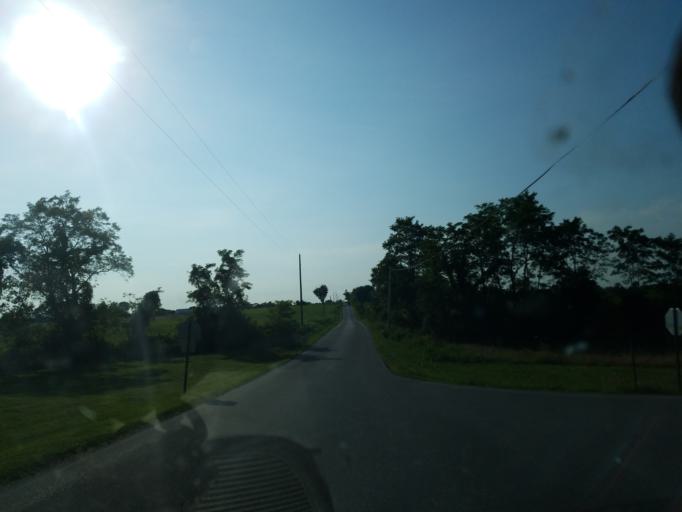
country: US
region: Ohio
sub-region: Adams County
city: West Union
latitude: 38.8788
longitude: -83.4896
